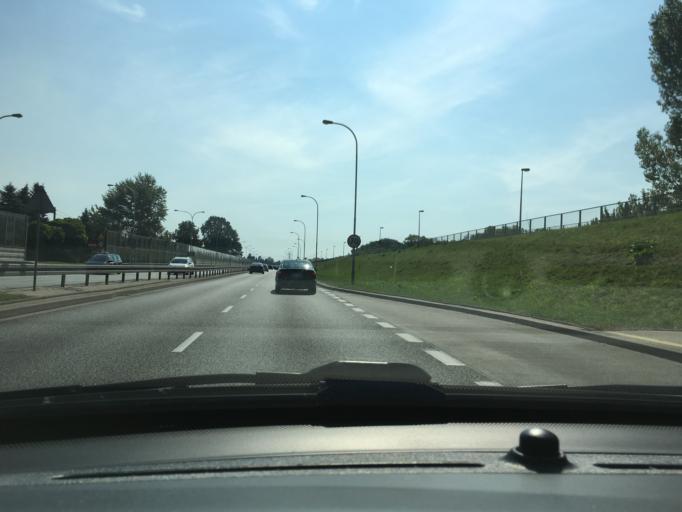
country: PL
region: Masovian Voivodeship
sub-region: Warszawa
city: Praga Poludnie
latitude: 52.2112
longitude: 21.1055
